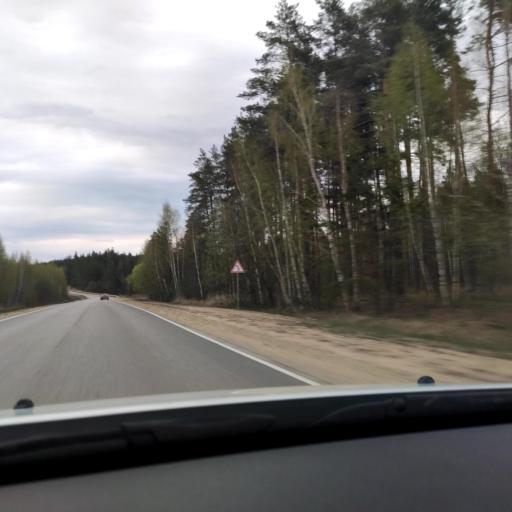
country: RU
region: Lipetsk
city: Zadonsk
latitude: 52.4227
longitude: 38.9477
